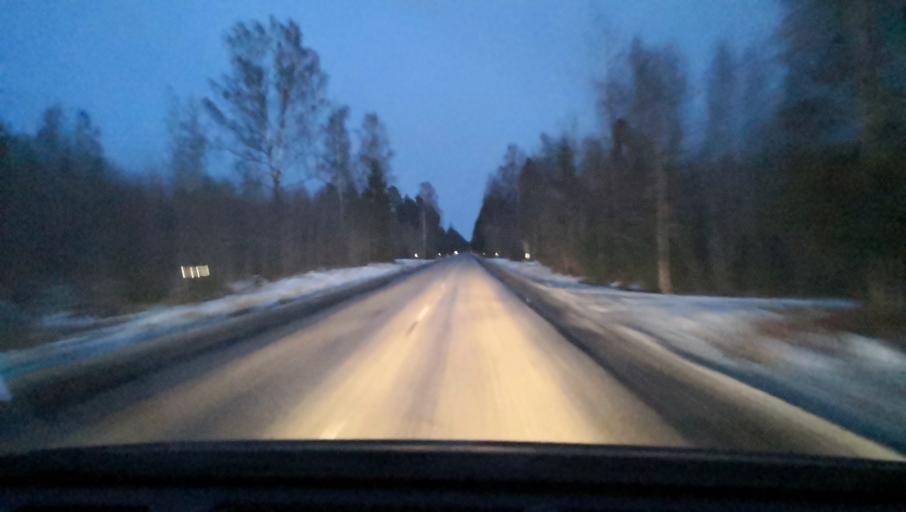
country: SE
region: Vaestmanland
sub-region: Sala Kommun
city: Sala
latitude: 59.8470
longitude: 16.4854
